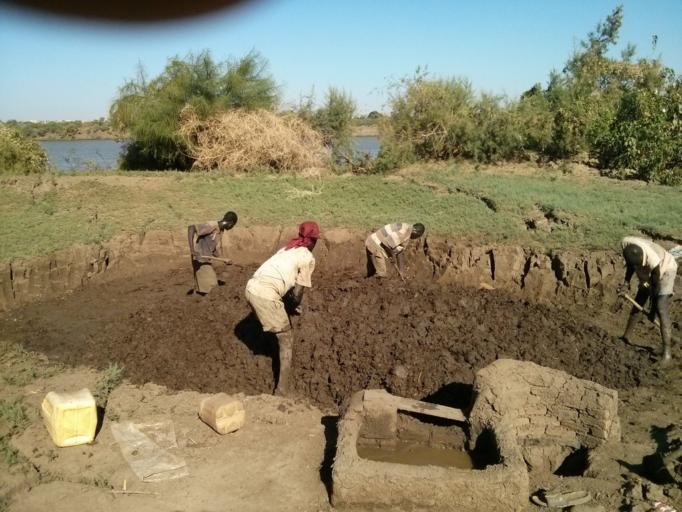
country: SD
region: Khartoum
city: Omdurman
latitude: 15.6306
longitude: 32.5056
